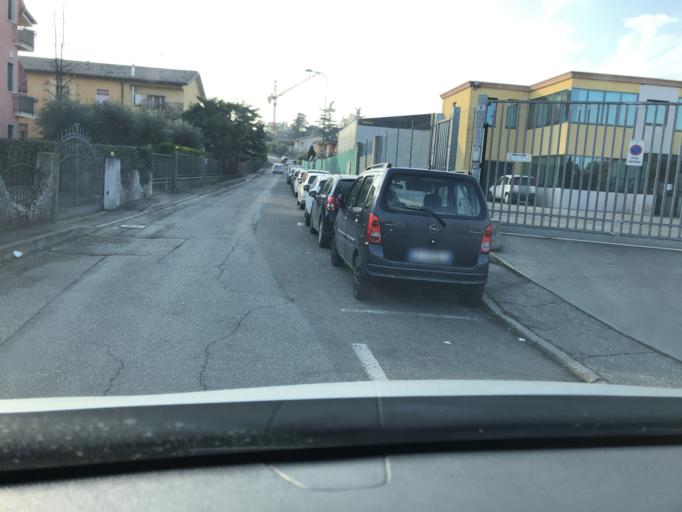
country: IT
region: Veneto
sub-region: Provincia di Verona
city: Sommacampagna
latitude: 45.4139
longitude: 10.8526
